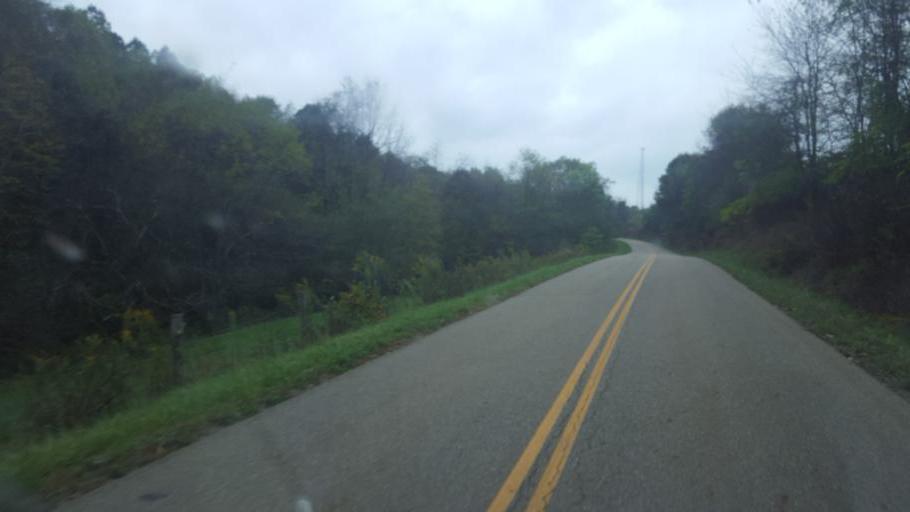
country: US
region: Ohio
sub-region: Carroll County
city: Carrollton
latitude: 40.4671
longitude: -81.0369
